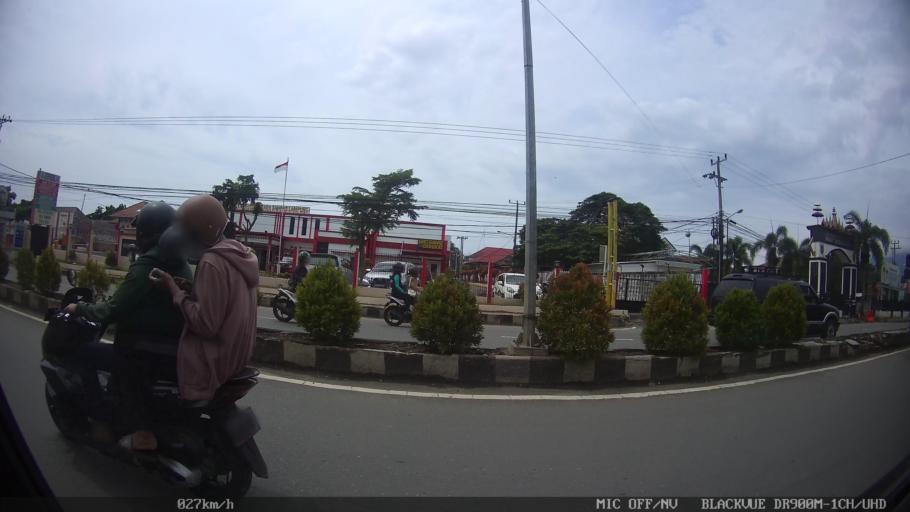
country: ID
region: Lampung
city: Kedaton
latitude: -5.3739
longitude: 105.2239
